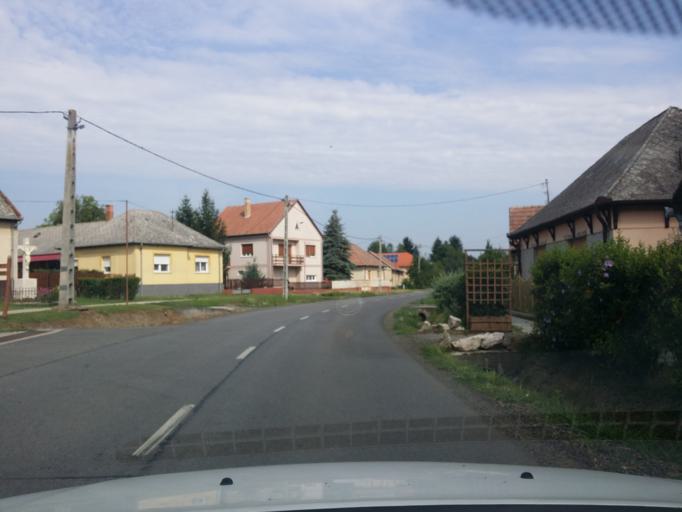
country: HU
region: Pest
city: Acsa
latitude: 47.7777
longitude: 19.3654
